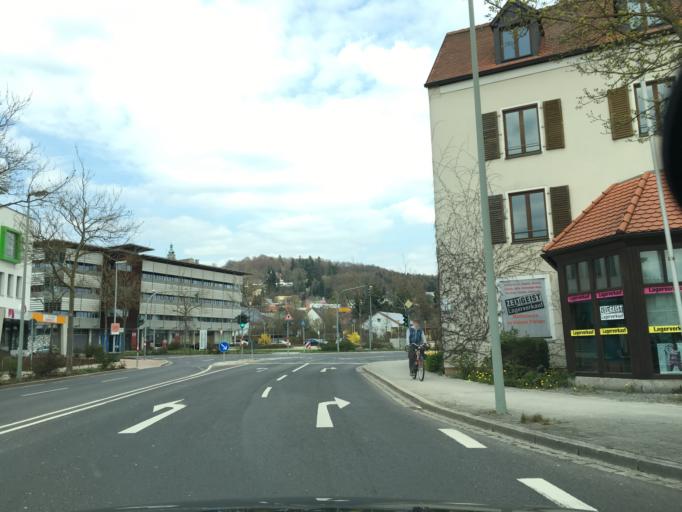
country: DE
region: Bavaria
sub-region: Upper Palatinate
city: Amberg
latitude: 49.4438
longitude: 11.8683
